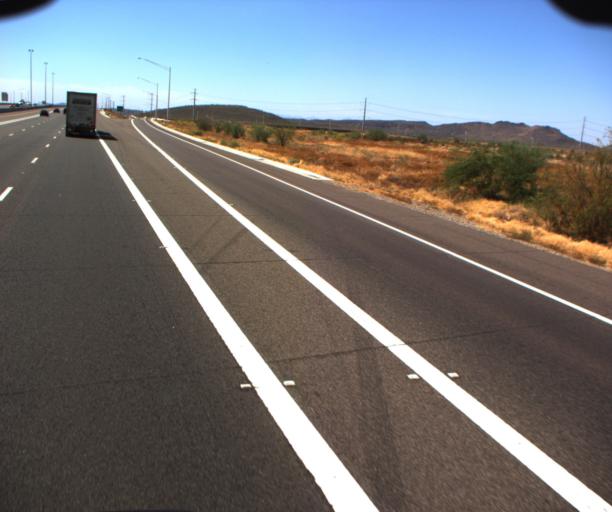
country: US
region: Arizona
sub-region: Maricopa County
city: Anthem
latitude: 33.7751
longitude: -112.1308
